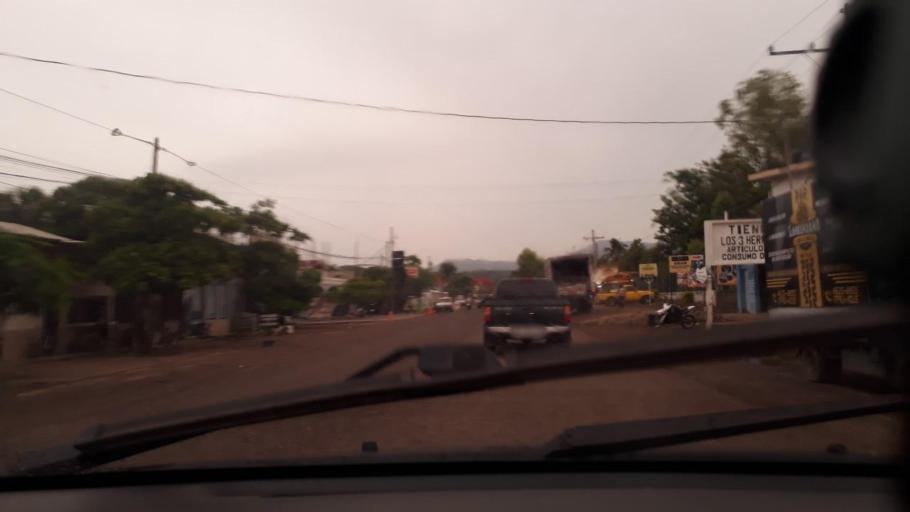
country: GT
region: Jutiapa
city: Asuncion Mita
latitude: 14.2901
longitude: -89.7211
